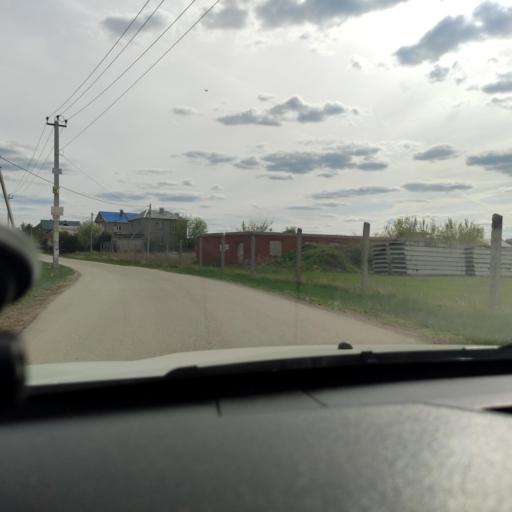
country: RU
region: Samara
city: Kinel'
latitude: 53.1669
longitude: 50.6406
